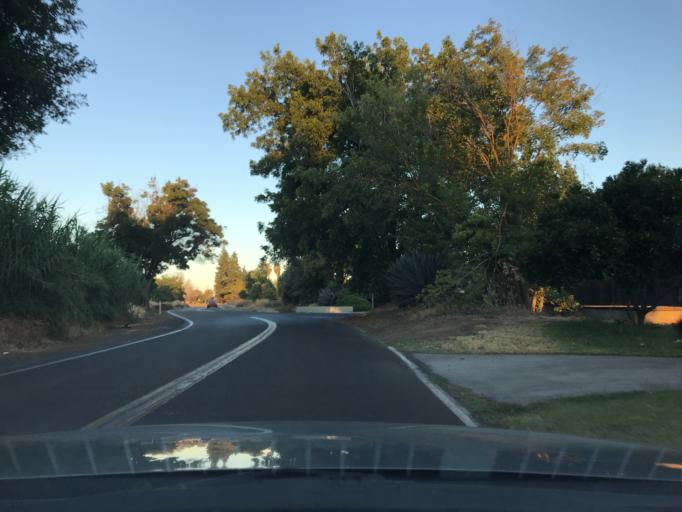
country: US
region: California
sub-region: Merced County
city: Merced
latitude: 37.3091
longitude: -120.4992
